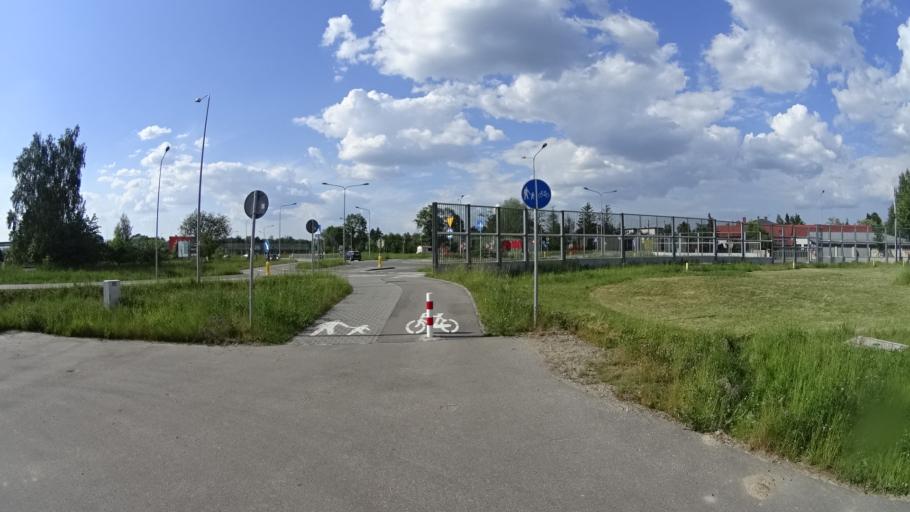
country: PL
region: Masovian Voivodeship
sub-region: Powiat pruszkowski
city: Nadarzyn
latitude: 52.0914
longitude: 20.8149
